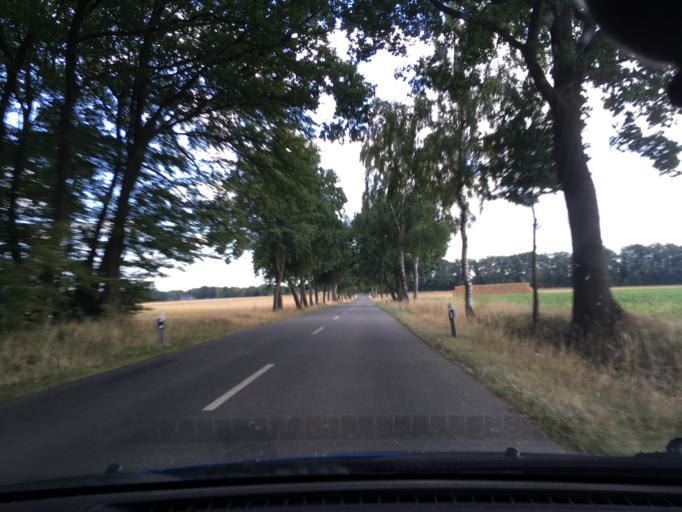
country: DE
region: Lower Saxony
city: Wriedel
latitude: 53.0394
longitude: 10.2703
